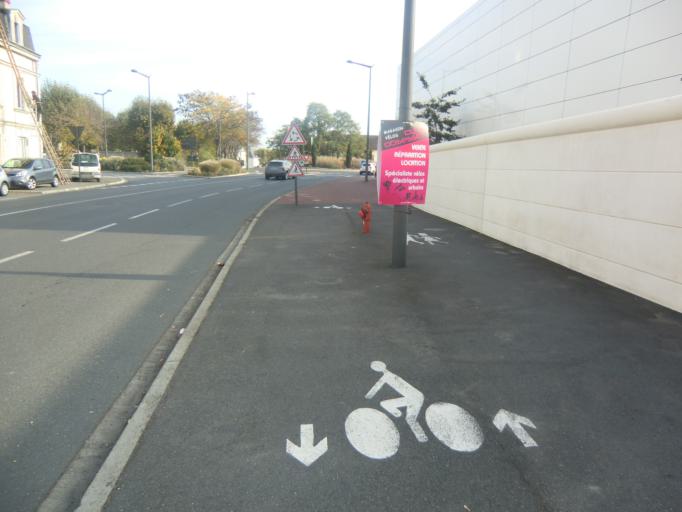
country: FR
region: Pays de la Loire
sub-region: Departement de Maine-et-Loire
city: Saumur
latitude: 47.2630
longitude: -0.0913
